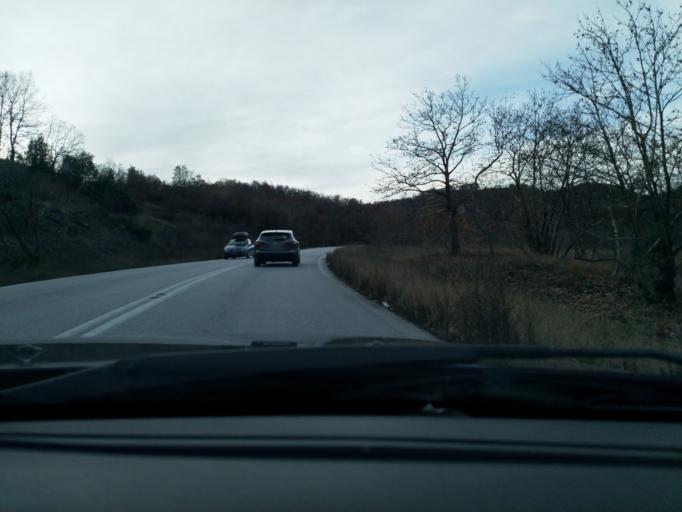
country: GR
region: Thessaly
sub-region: Trikala
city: Kastraki
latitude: 39.7414
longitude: 21.5280
